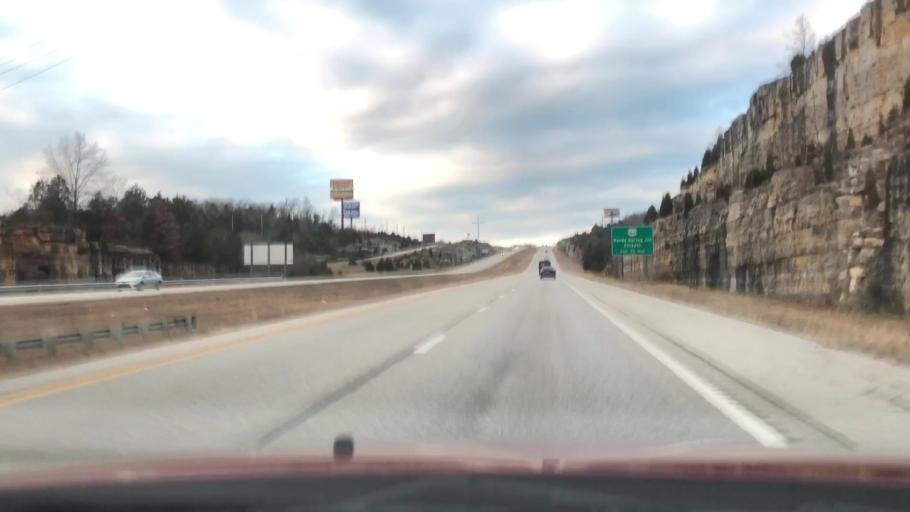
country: US
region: Missouri
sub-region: Taney County
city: Merriam Woods
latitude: 36.7367
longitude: -93.2211
